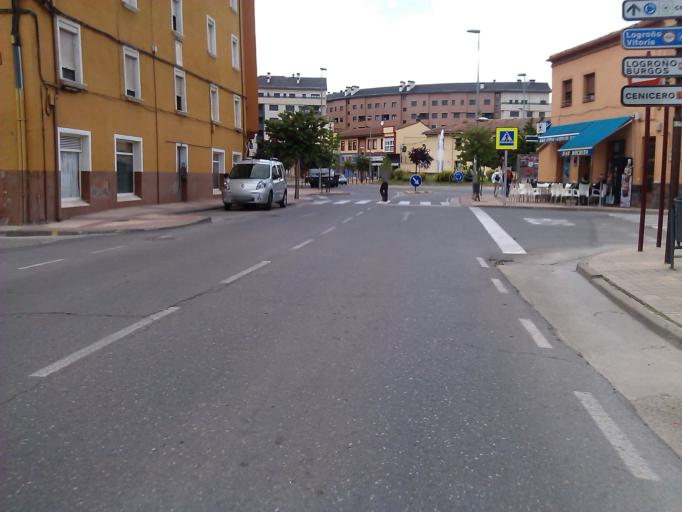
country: ES
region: La Rioja
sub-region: Provincia de La Rioja
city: Najera
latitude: 42.4182
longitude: -2.7248
